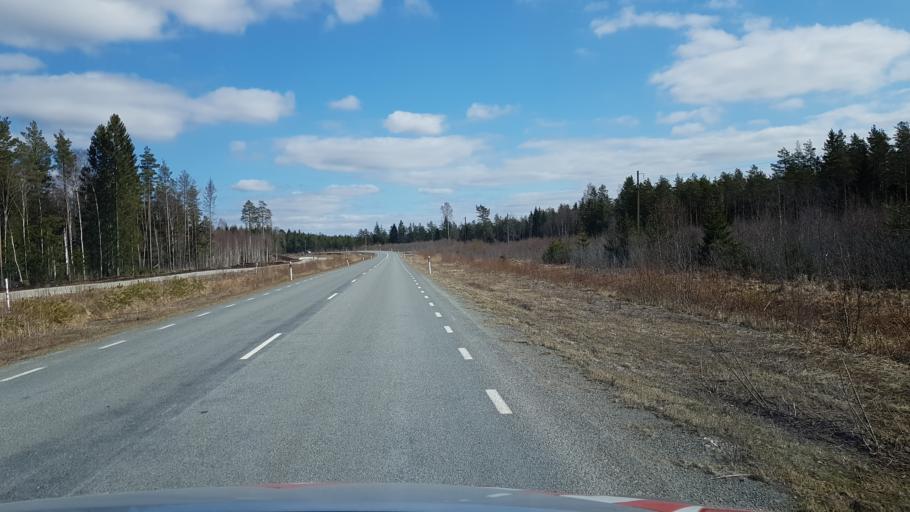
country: EE
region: Laeaene-Virumaa
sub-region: Tapa vald
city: Tapa
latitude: 59.2774
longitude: 25.8966
